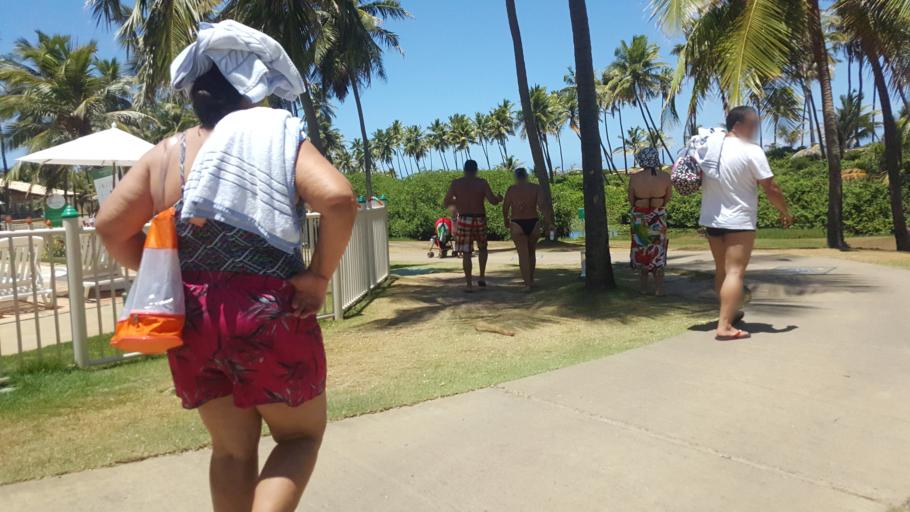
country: BR
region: Bahia
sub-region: Mata De Sao Joao
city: Mata de Sao Joao
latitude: -12.4421
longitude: -37.9217
